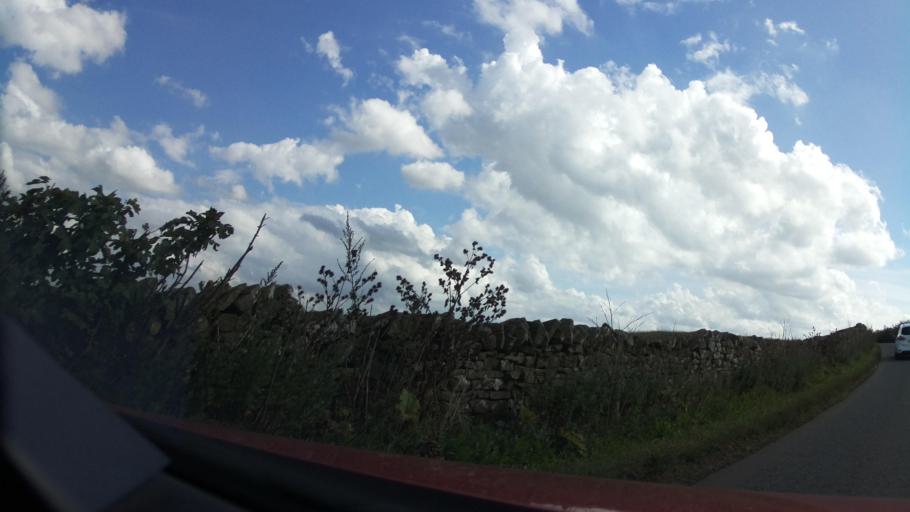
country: GB
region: England
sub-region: North Yorkshire
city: Leyburn
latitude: 54.3261
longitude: -1.8250
